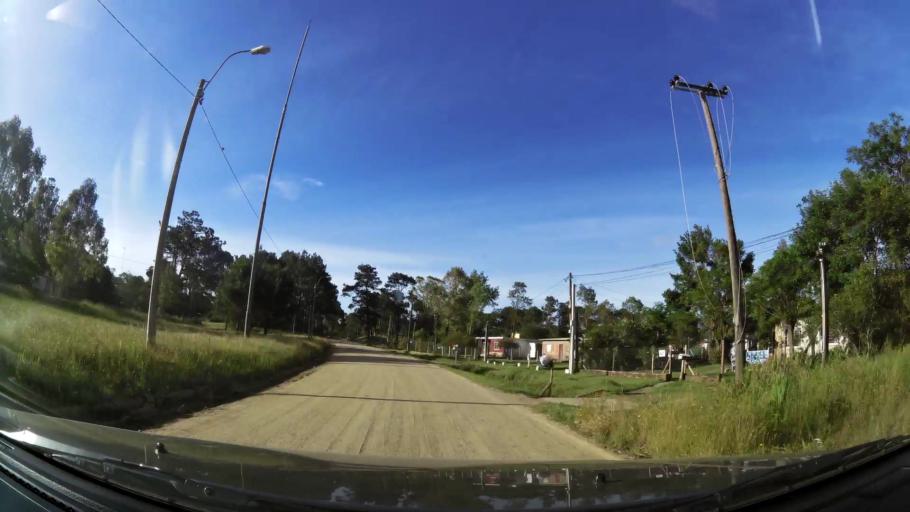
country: UY
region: Canelones
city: Empalme Olmos
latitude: -34.7737
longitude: -55.8565
